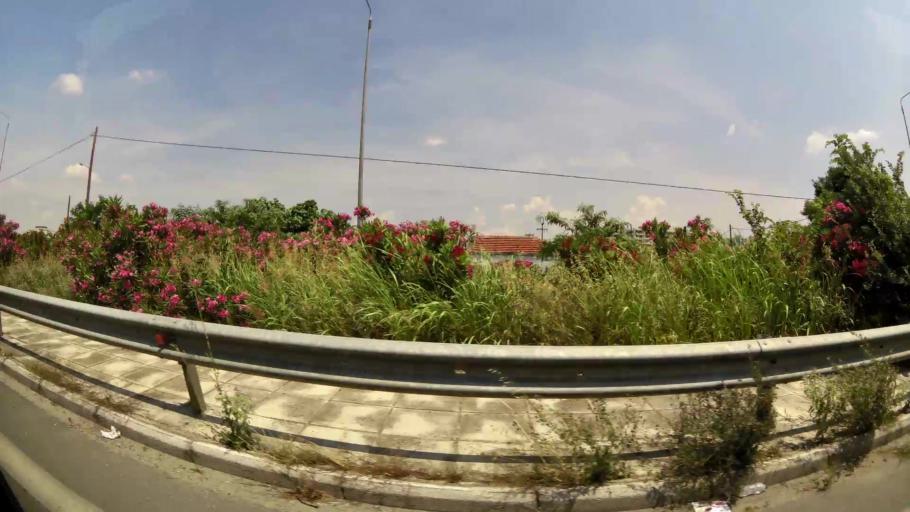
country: GR
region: Central Macedonia
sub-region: Nomos Thessalonikis
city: Menemeni
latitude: 40.6513
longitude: 22.9043
